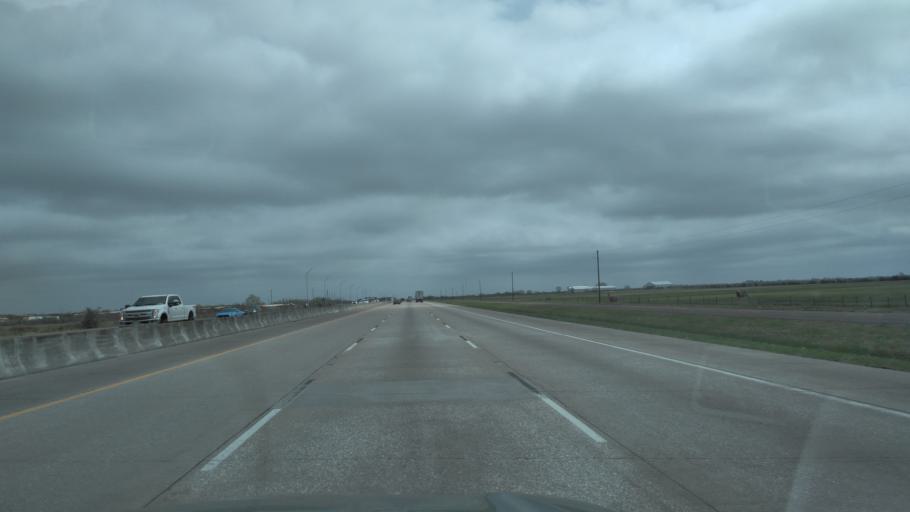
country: US
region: Texas
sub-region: Chambers County
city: Winnie
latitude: 29.8332
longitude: -94.5238
